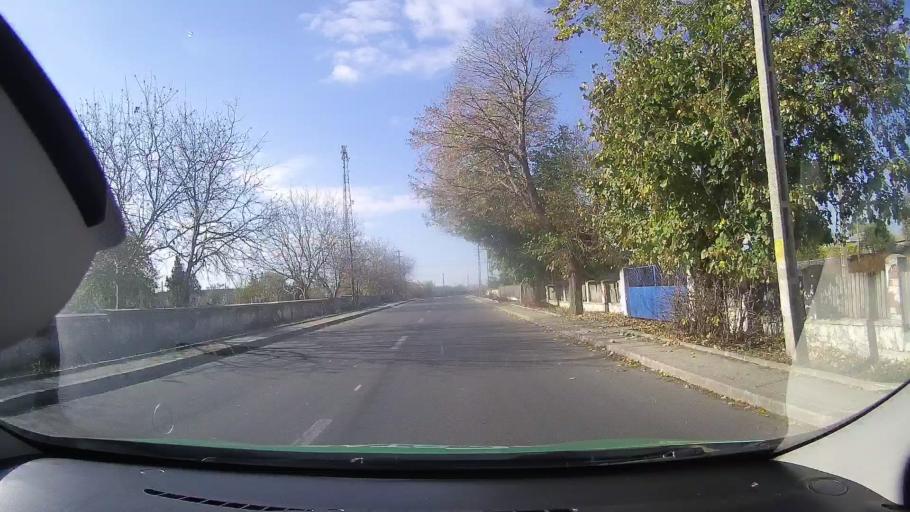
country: RO
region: Tulcea
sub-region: Comuna Valea Nucarilor
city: Valea Nucarilor
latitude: 45.0422
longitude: 28.9328
